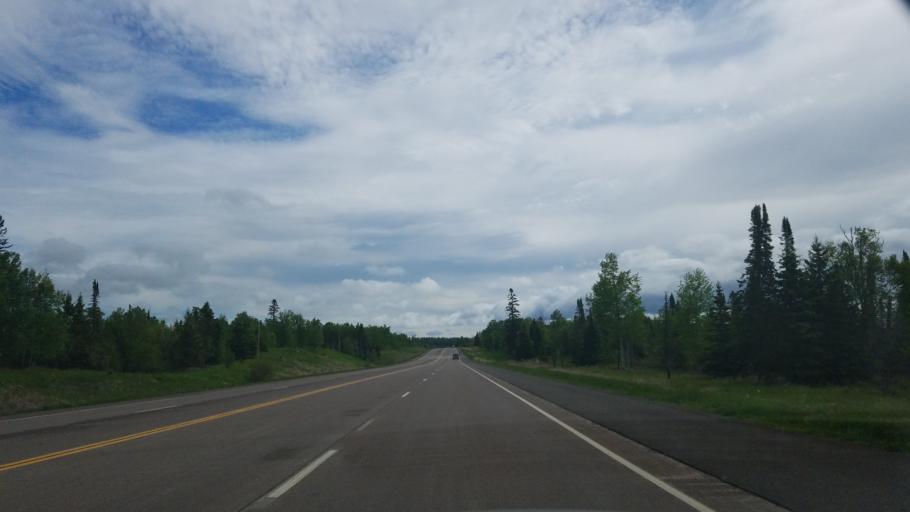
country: US
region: Minnesota
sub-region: Lake County
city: Two Harbors
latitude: 47.1280
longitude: -91.4896
